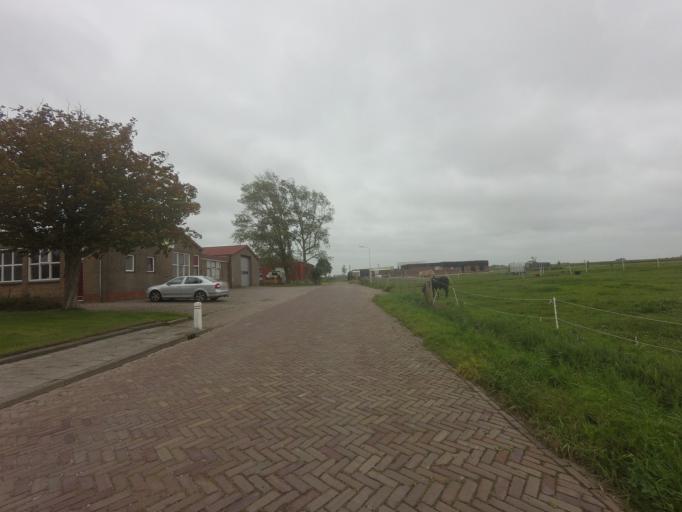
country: NL
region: Friesland
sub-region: Gemeente Ferwerderadiel
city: Ferwert
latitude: 53.3494
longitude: 5.8612
